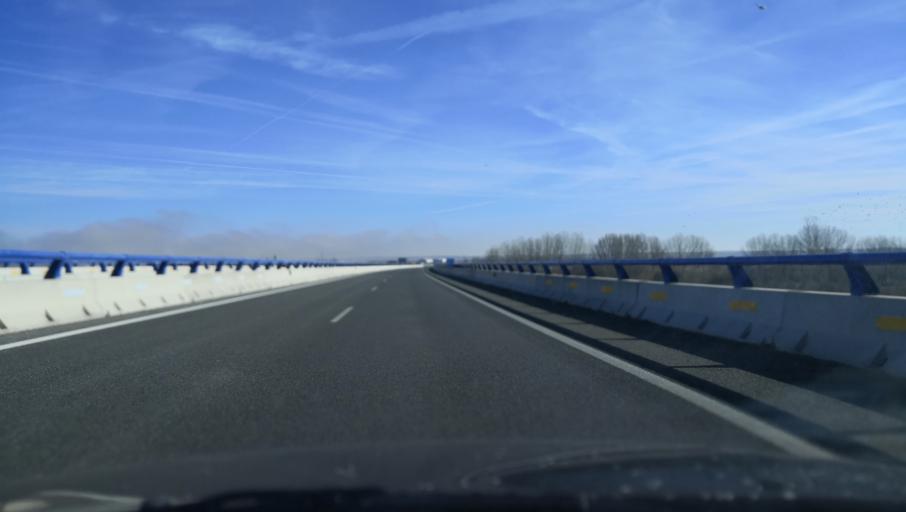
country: ES
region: Castille and Leon
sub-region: Provincia de Salamanca
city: Encinas de Abajo
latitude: 40.9266
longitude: -5.4901
